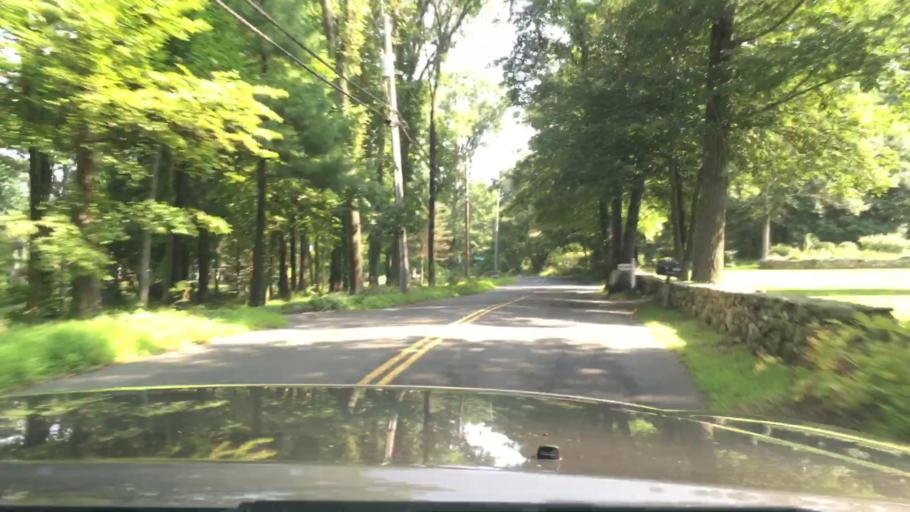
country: US
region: Connecticut
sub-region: Fairfield County
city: Georgetown
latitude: 41.2415
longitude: -73.4574
